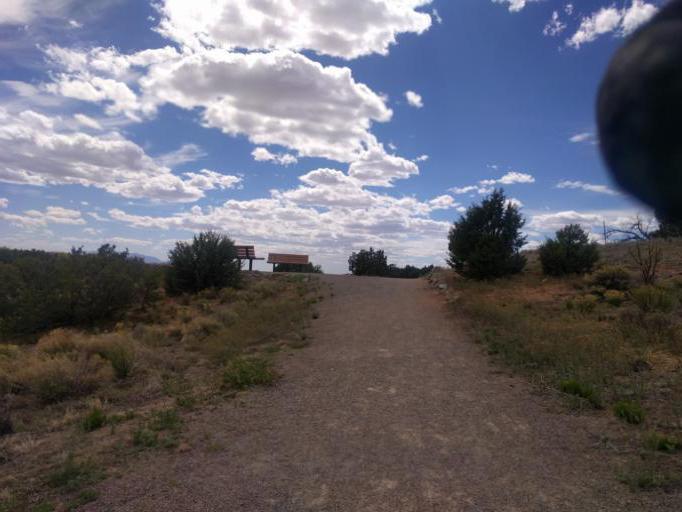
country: US
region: New Mexico
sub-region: Santa Fe County
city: Agua Fria
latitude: 35.5991
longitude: -105.9940
